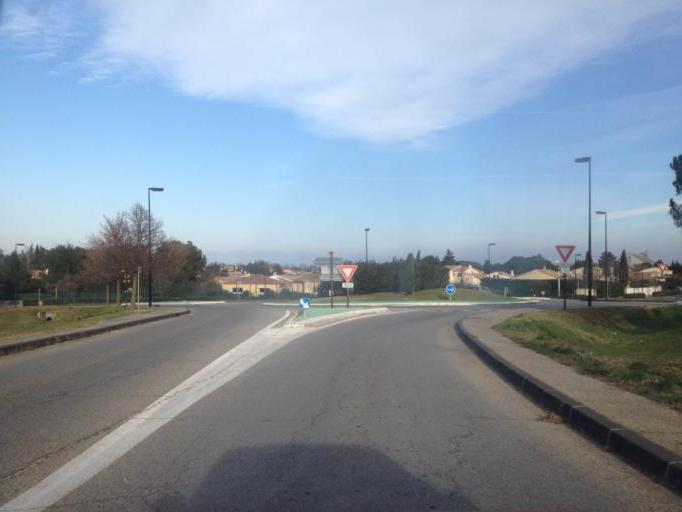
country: FR
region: Provence-Alpes-Cote d'Azur
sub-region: Departement du Vaucluse
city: Orange
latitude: 44.1208
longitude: 4.8191
